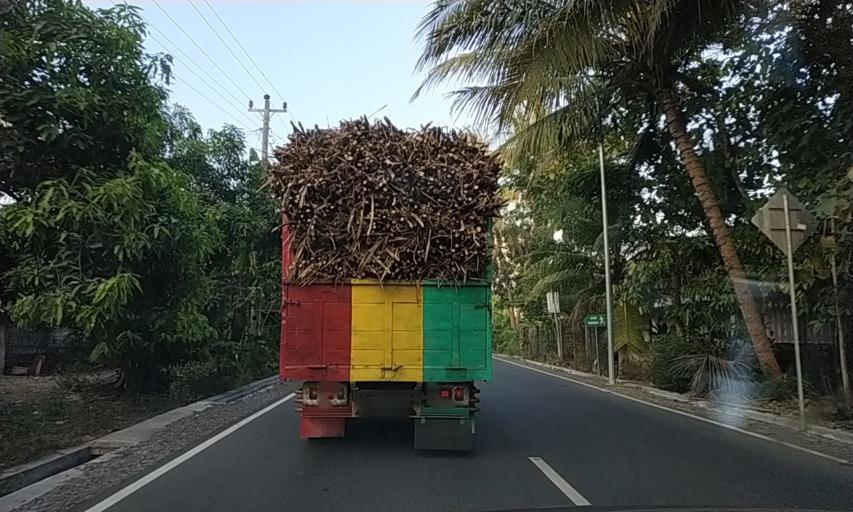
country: ID
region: Daerah Istimewa Yogyakarta
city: Srandakan
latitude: -7.8841
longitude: 110.0451
